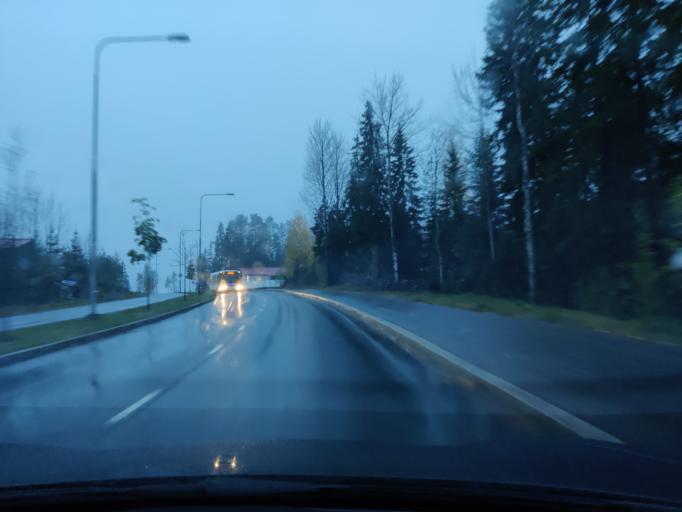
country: FI
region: Northern Savo
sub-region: Kuopio
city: Kuopio
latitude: 62.8296
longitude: 27.7028
